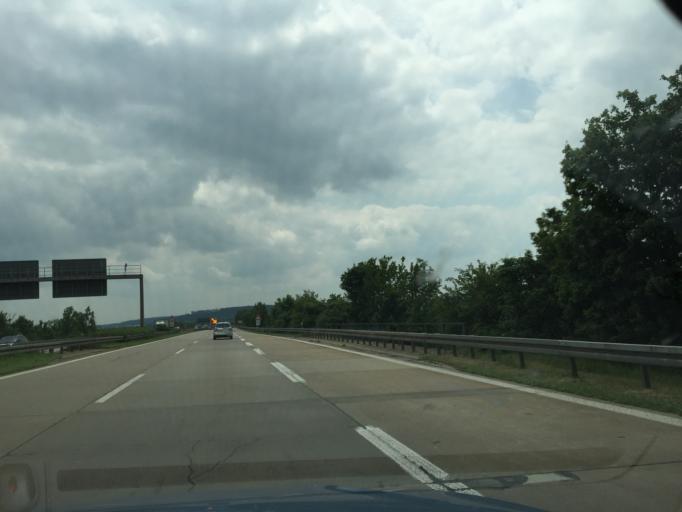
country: DE
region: Bavaria
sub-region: Regierungsbezirk Mittelfranken
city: Schnelldorf
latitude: 49.1941
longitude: 10.2363
